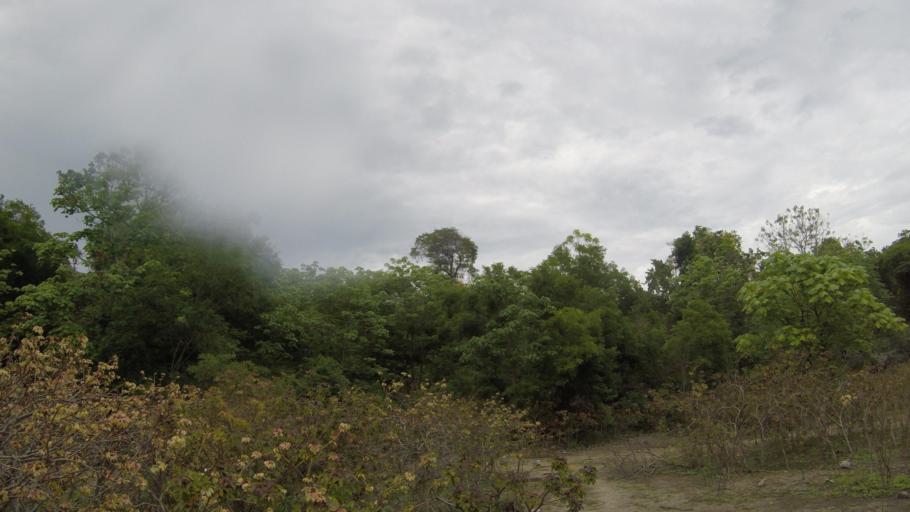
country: TL
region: Lautem
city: Lospalos
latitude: -8.3542
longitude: 127.0527
